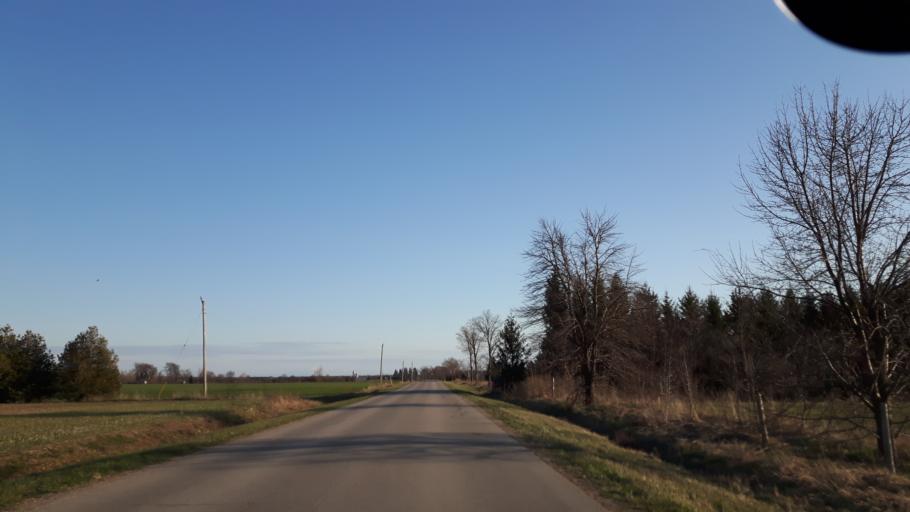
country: CA
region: Ontario
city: Goderich
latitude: 43.6509
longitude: -81.6846
